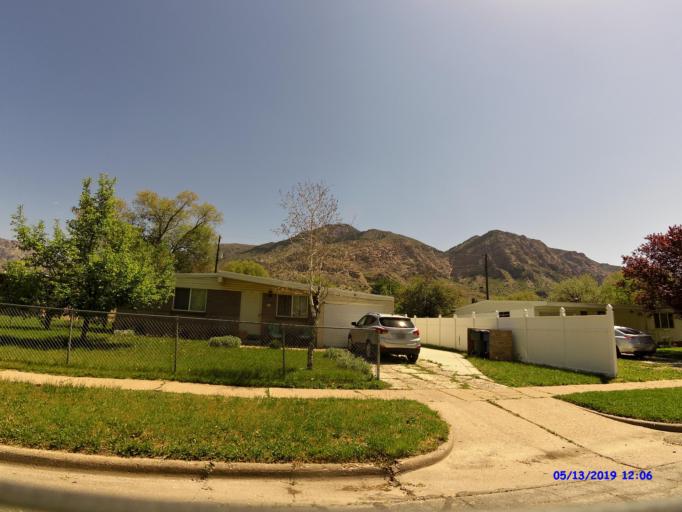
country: US
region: Utah
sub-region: Weber County
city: Harrisville
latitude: 41.2745
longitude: -111.9638
